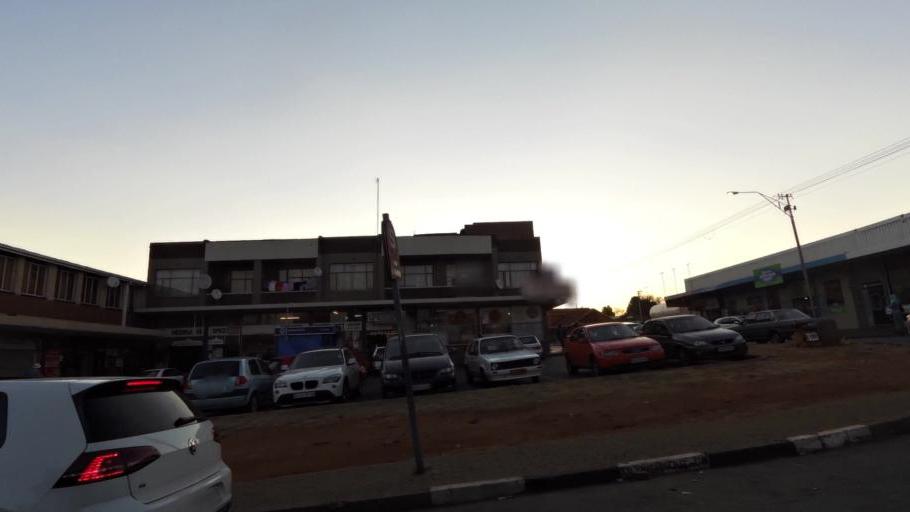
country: ZA
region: Gauteng
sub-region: City of Johannesburg Metropolitan Municipality
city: Roodepoort
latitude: -26.1875
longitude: 27.9534
